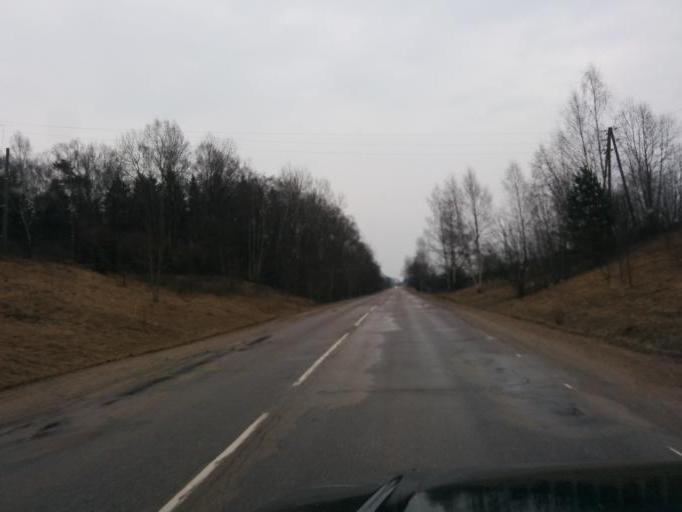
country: LV
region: Salaspils
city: Salaspils
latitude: 56.8212
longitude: 24.4268
